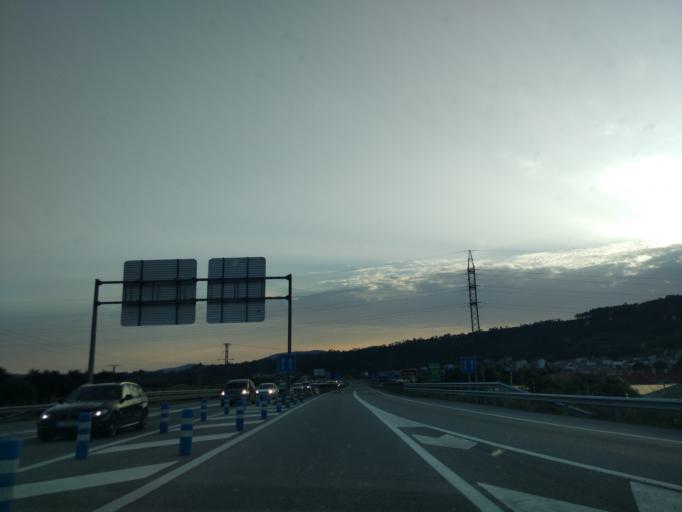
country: ES
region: Galicia
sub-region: Provincia da Coruna
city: Padron
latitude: 42.7313
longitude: -8.6597
